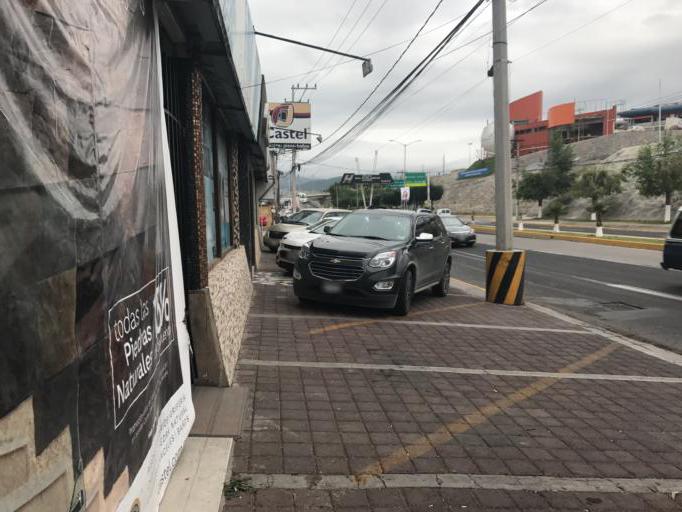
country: MX
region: Hidalgo
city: Pachuca de Soto
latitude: 20.1055
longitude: -98.7585
